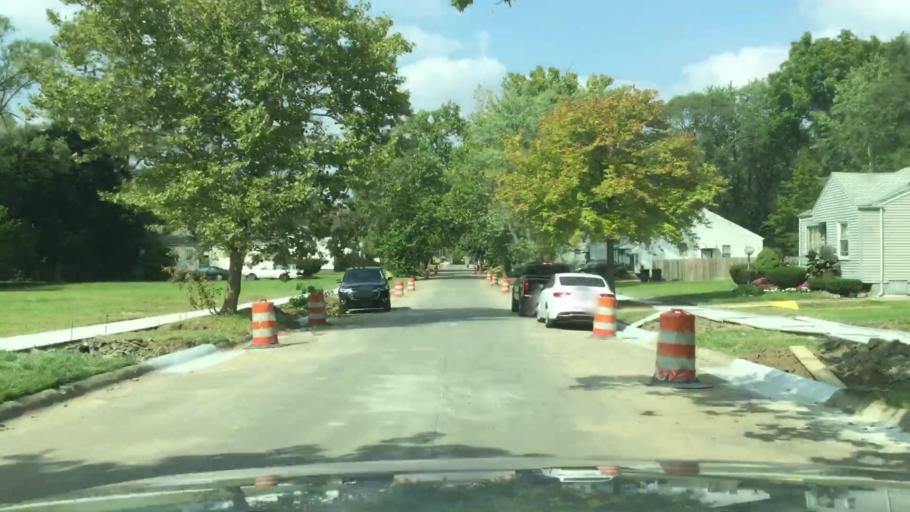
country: US
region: Michigan
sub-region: Wayne County
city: Dearborn
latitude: 42.3617
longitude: -83.2003
